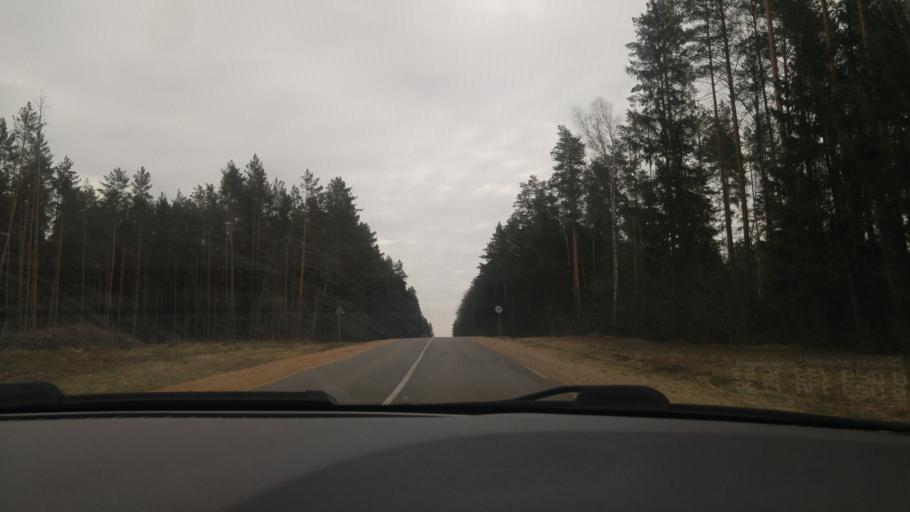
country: BY
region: Minsk
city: Chervyen'
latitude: 53.7357
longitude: 28.3072
